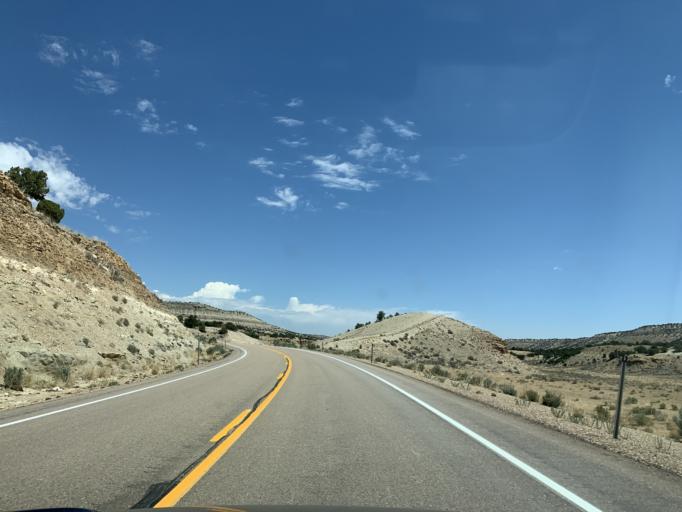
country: US
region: Utah
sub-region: Duchesne County
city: Duchesne
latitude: 39.9360
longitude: -110.2170
